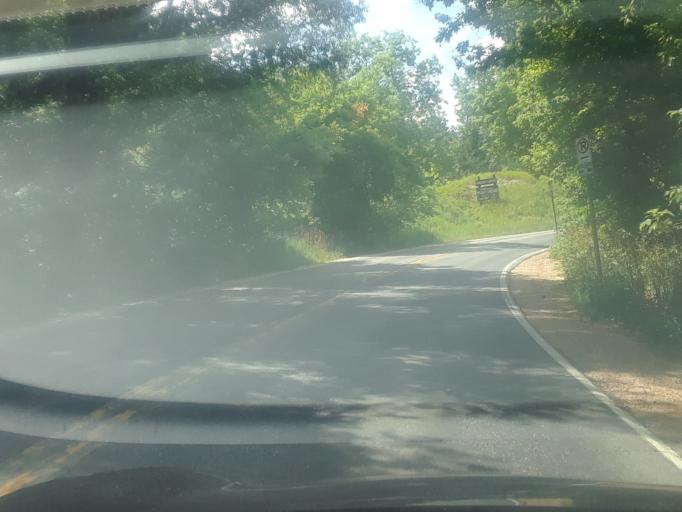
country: US
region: Colorado
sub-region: Boulder County
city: Boulder
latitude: 40.0205
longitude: -105.2988
